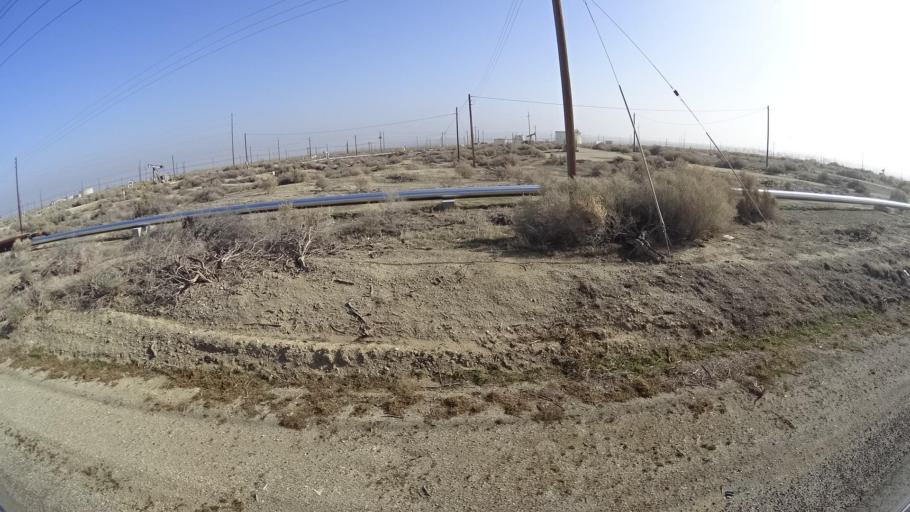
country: US
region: California
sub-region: Kern County
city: Taft Heights
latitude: 35.2170
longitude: -119.5697
